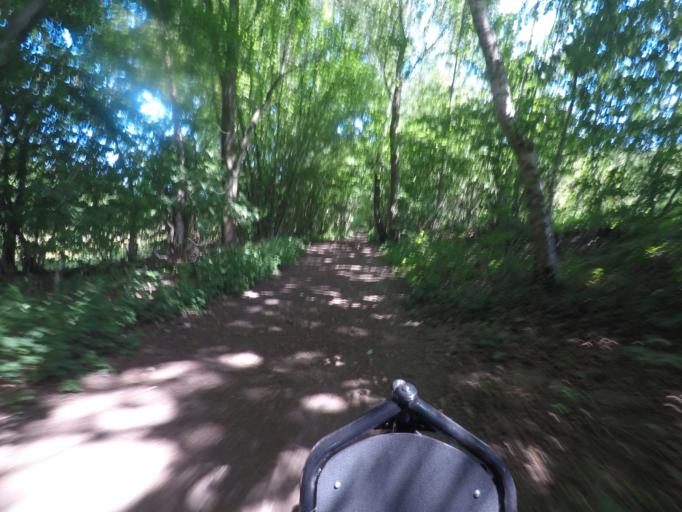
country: DE
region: Schleswig-Holstein
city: Stapelfeld
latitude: 53.6171
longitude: 10.1799
